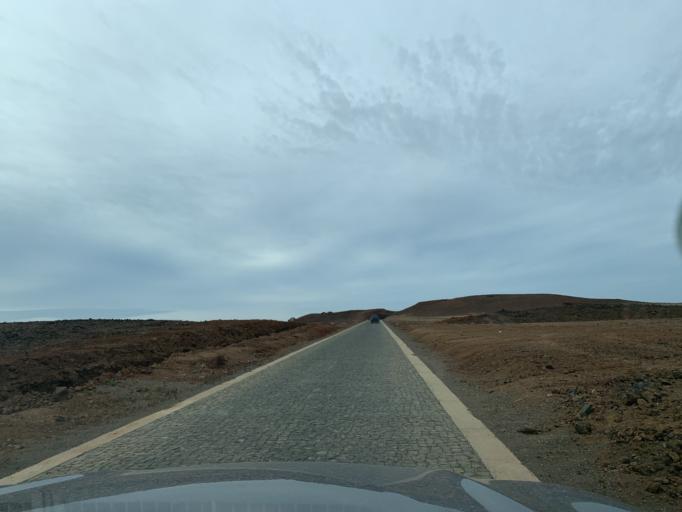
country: CV
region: Porto Novo
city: Porto Novo
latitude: 16.9684
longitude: -25.2734
